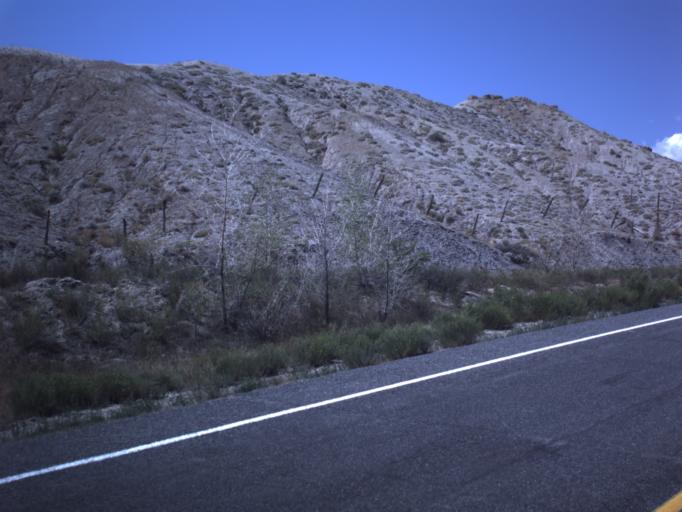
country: US
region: Utah
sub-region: Emery County
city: Orangeville
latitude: 39.2130
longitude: -111.0566
